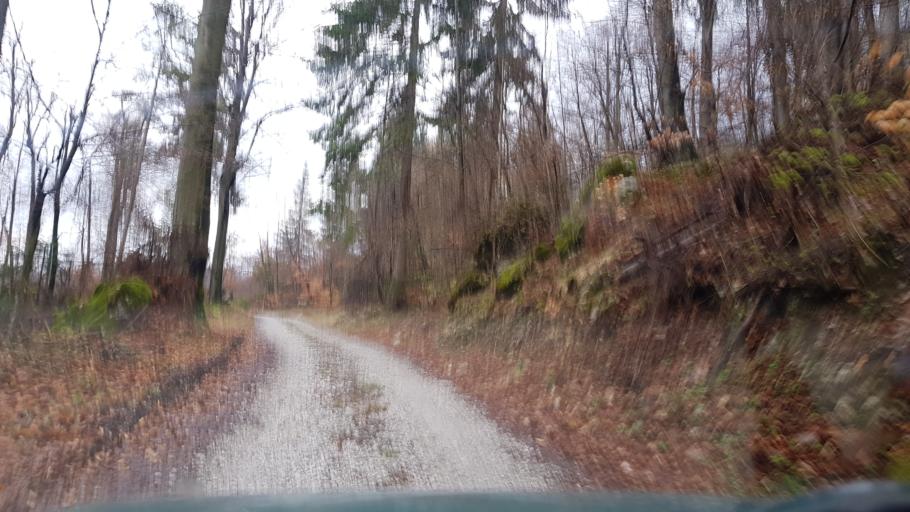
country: SI
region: Cerkno
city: Cerkno
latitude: 46.1324
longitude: 13.8660
